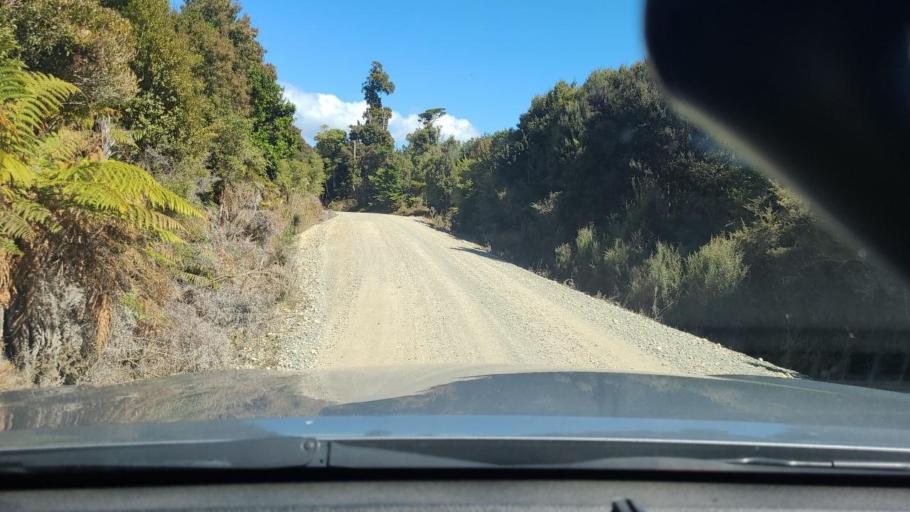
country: NZ
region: Southland
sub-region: Southland District
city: Riverton
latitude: -46.1452
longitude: 167.5017
